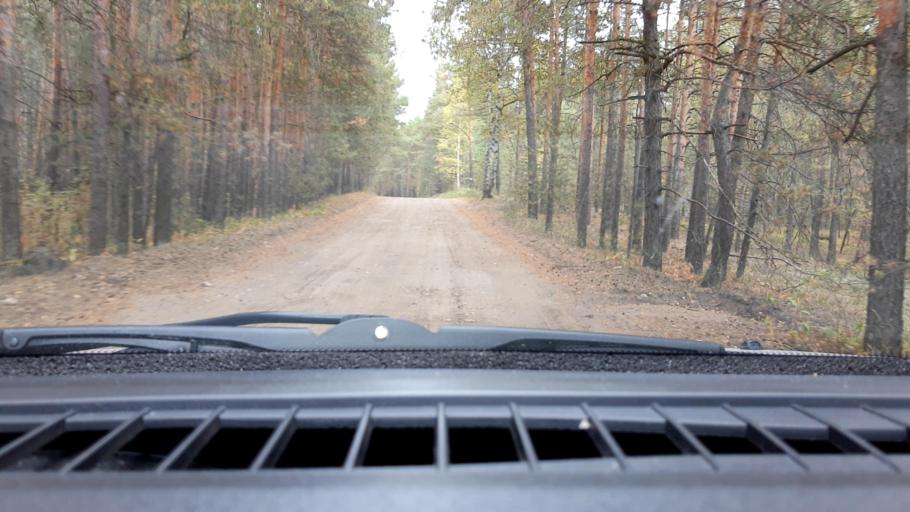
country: RU
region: Nizjnij Novgorod
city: Gorbatovka
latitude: 56.3170
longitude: 43.6956
